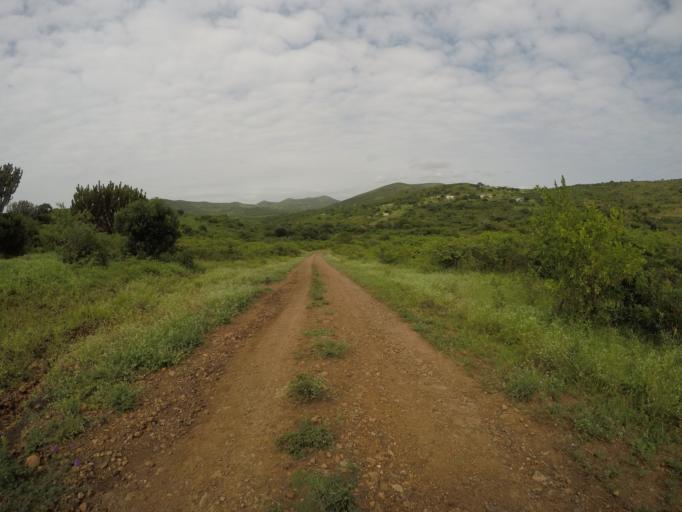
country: ZA
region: KwaZulu-Natal
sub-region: uThungulu District Municipality
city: Empangeni
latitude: -28.6259
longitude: 31.8963
